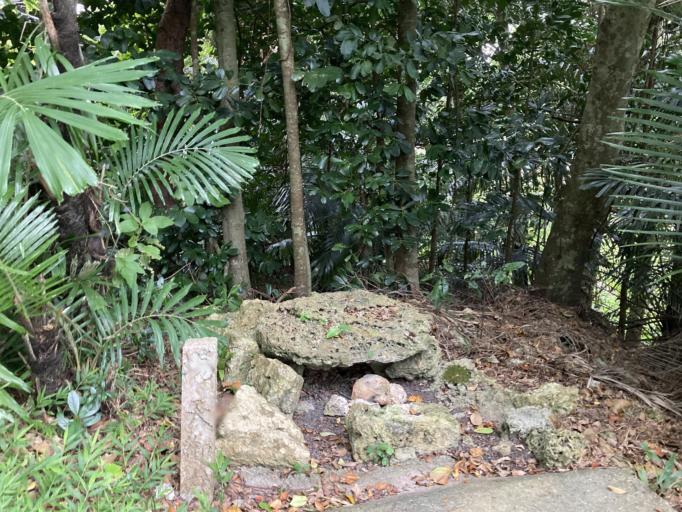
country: JP
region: Okinawa
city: Tomigusuku
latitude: 26.1692
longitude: 127.7735
